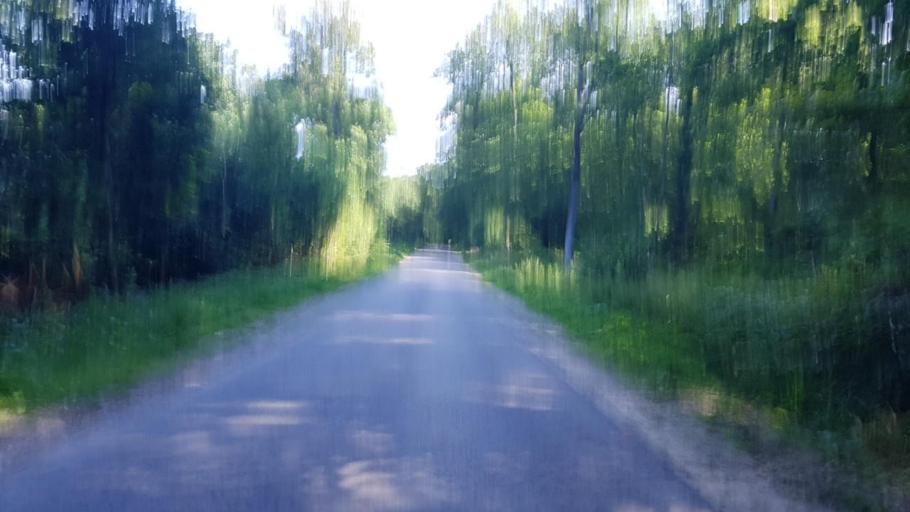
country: FR
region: Picardie
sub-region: Departement de l'Oise
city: Pont-Sainte-Maxence
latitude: 49.2834
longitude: 2.6234
